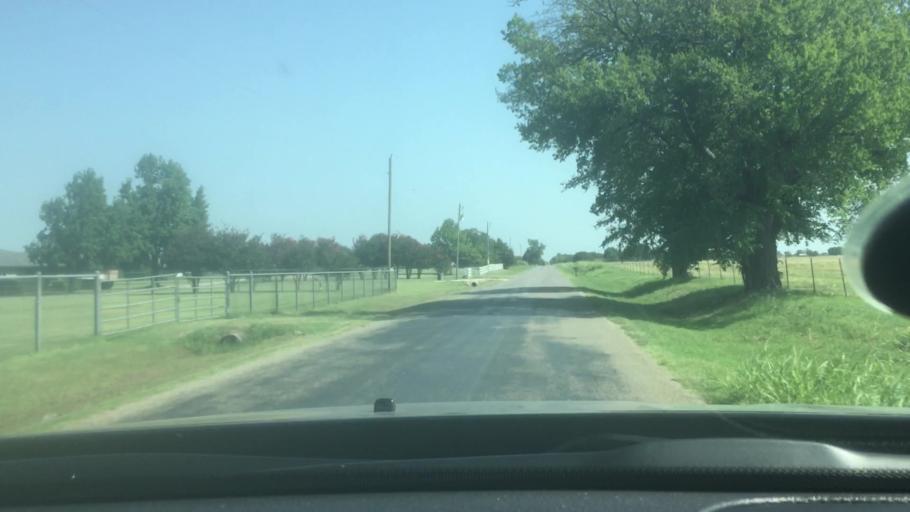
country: US
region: Oklahoma
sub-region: Bryan County
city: Calera
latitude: 33.9844
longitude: -96.4656
